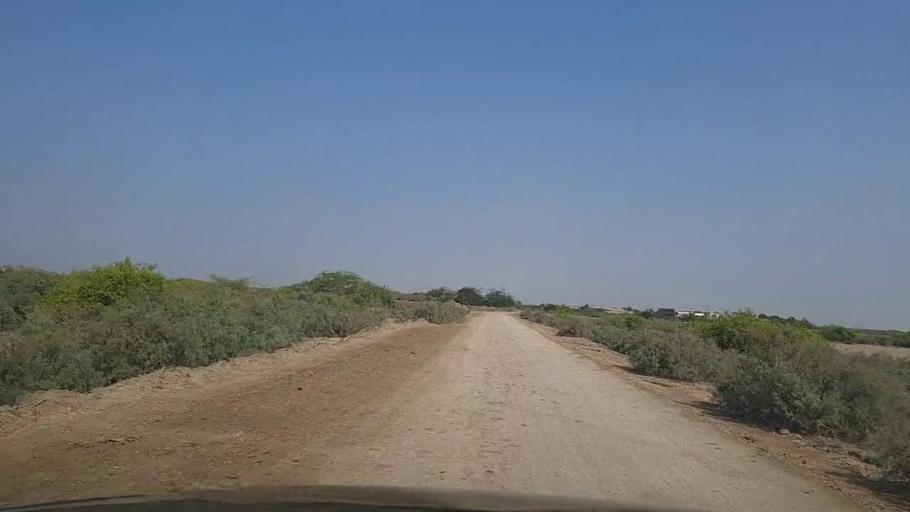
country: PK
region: Sindh
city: Thatta
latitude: 24.6458
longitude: 67.8166
